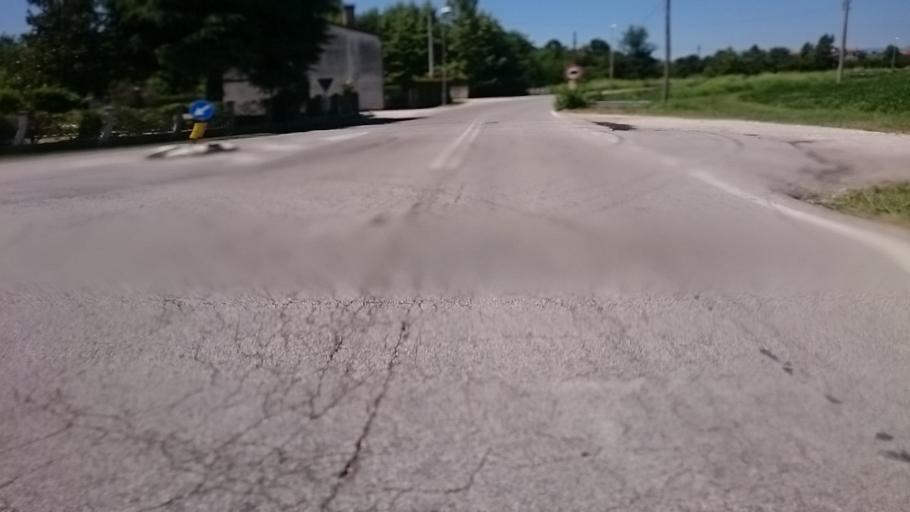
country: IT
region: Veneto
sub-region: Provincia di Padova
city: Campodarsego
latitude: 45.5116
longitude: 11.9336
